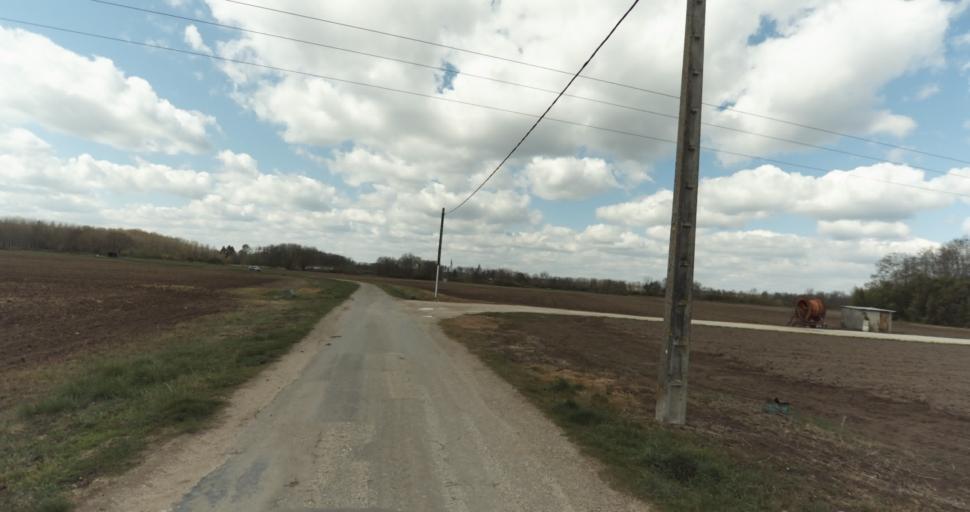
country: FR
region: Bourgogne
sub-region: Departement de la Cote-d'Or
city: Auxonne
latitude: 47.1797
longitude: 5.3786
